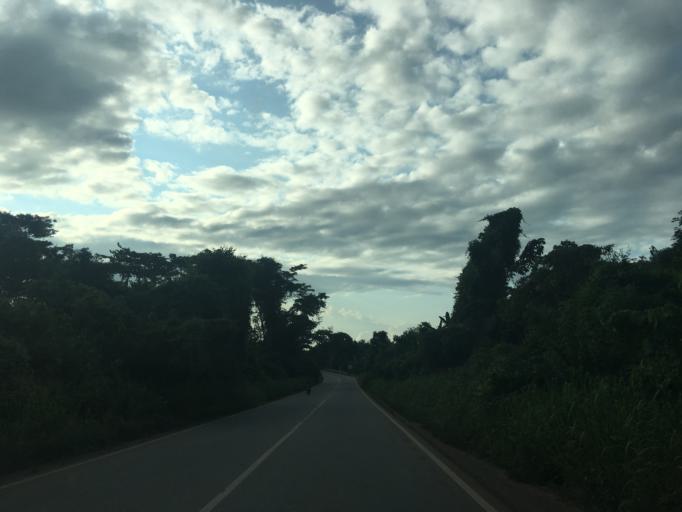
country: GH
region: Western
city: Bibiani
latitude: 6.3515
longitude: -2.2789
